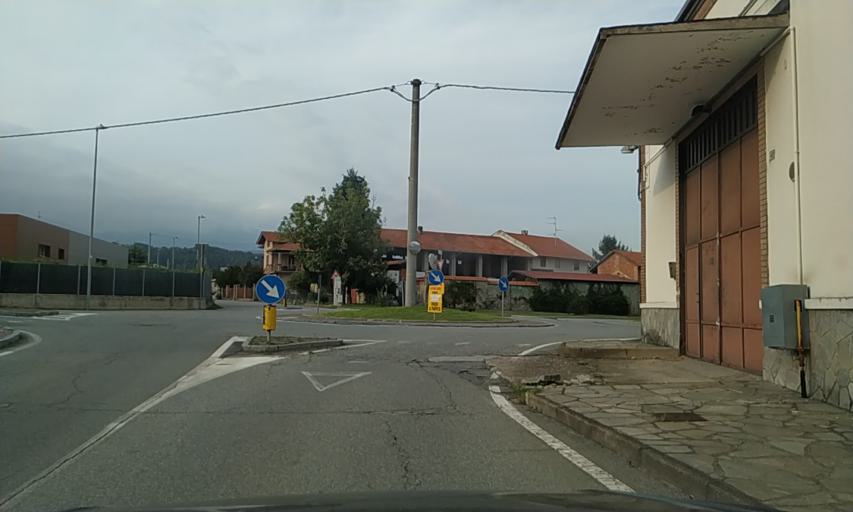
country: IT
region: Piedmont
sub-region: Provincia di Biella
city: Vigliano Biellese
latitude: 45.5567
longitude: 8.1190
